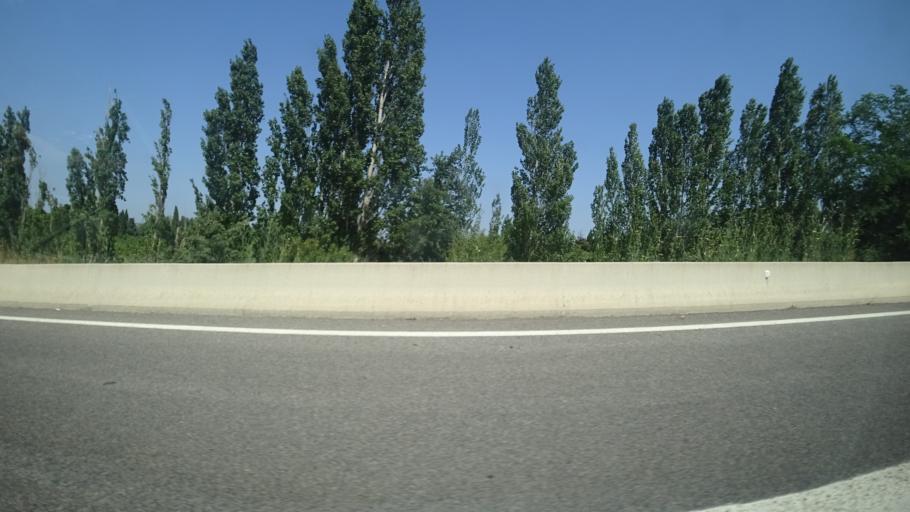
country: FR
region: Languedoc-Roussillon
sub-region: Departement des Pyrenees-Orientales
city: Ille-sur-Tet
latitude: 42.6649
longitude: 2.6029
